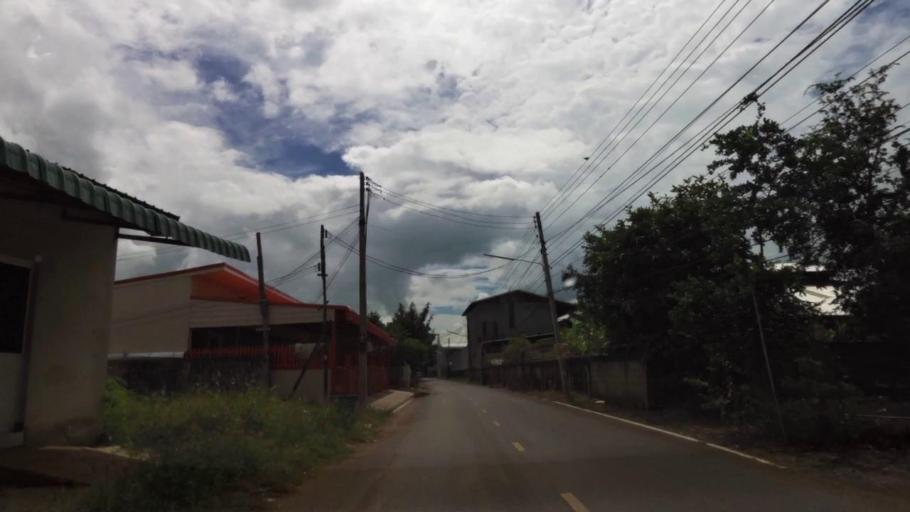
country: TH
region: Nakhon Sawan
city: Phai Sali
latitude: 15.5960
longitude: 100.6451
